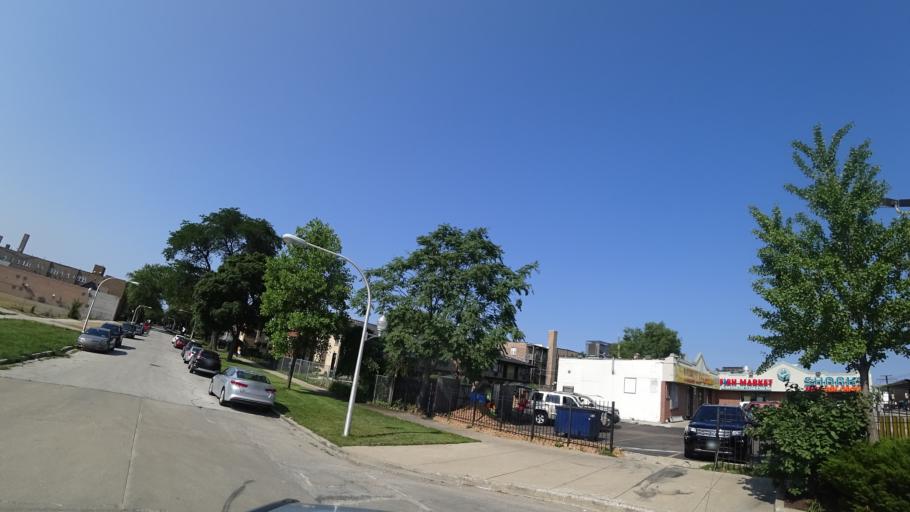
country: US
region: Illinois
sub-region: Cook County
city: Chicago
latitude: 41.7663
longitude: -87.5828
